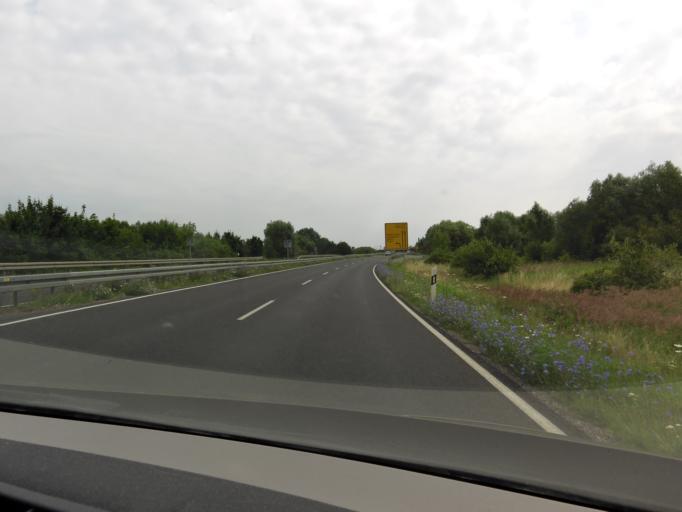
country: DE
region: Saxony-Anhalt
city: Wittenburg
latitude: 51.8420
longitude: 12.6311
